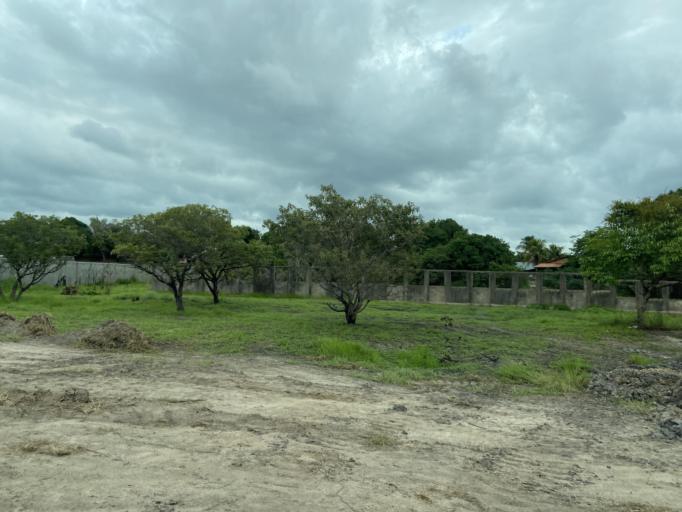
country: BR
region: Para
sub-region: Maraba
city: Maraba
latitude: -5.2938
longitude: -49.0645
